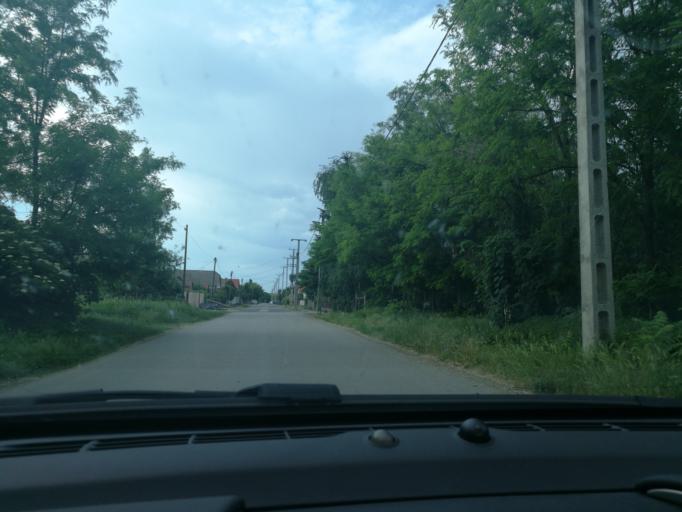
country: HU
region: Szabolcs-Szatmar-Bereg
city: Nyirpazony
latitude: 47.9409
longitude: 21.7968
